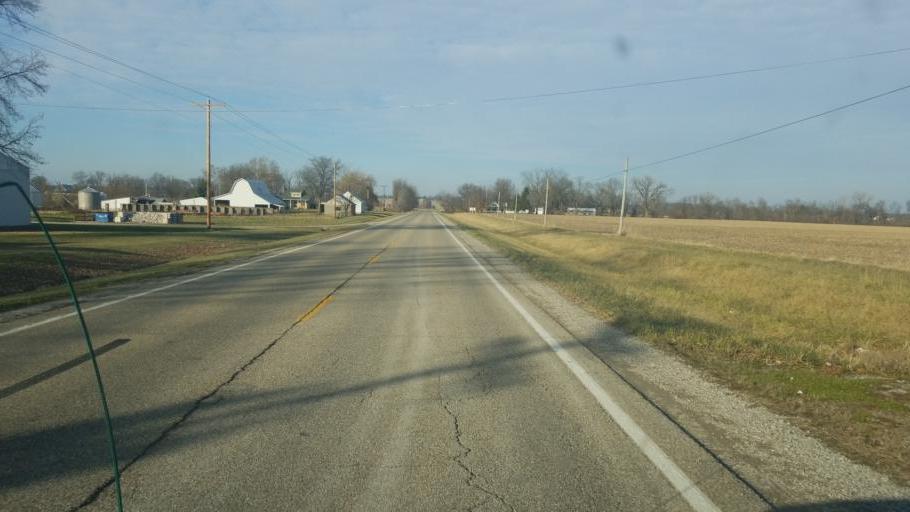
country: US
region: Illinois
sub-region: Lawrence County
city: Lawrenceville
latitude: 38.6341
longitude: -87.6941
